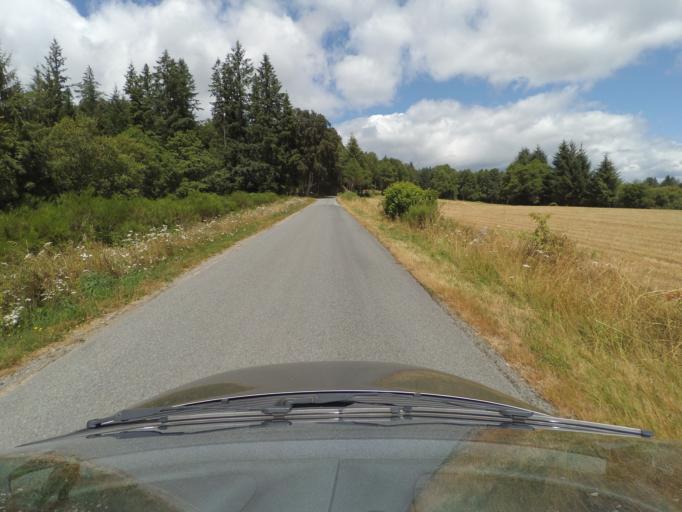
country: FR
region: Limousin
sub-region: Departement de la Creuse
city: Banize
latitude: 45.8003
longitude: 1.9311
